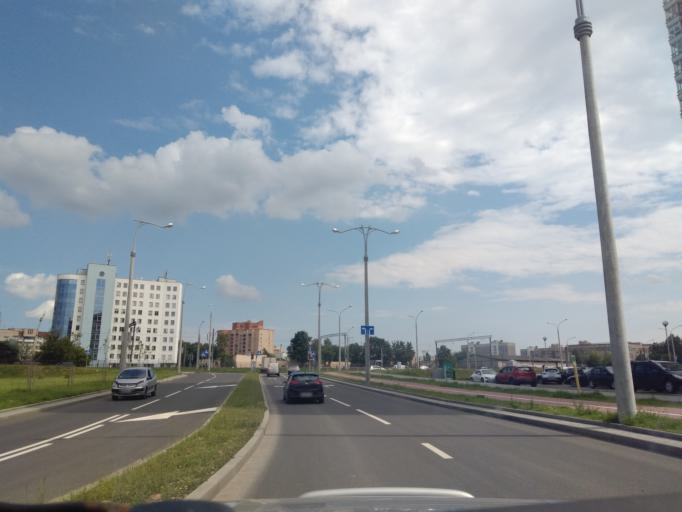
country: BY
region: Minsk
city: Minsk
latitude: 53.8713
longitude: 27.5595
